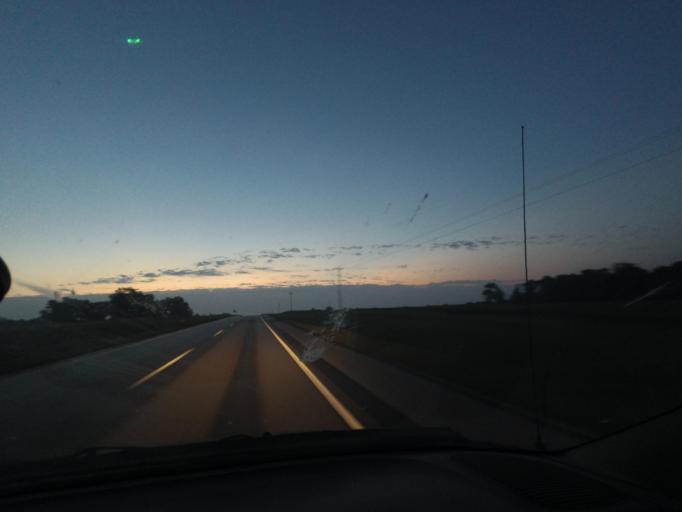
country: US
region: Missouri
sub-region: Linn County
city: Linneus
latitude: 39.7777
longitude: -93.2612
